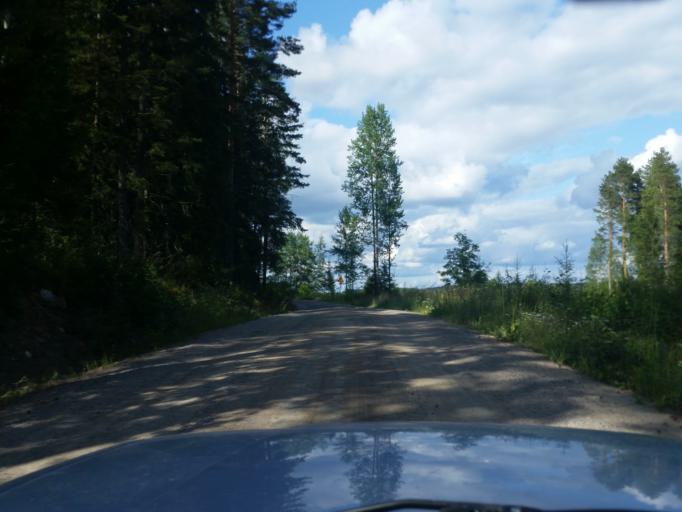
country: FI
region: Southern Savonia
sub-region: Savonlinna
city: Sulkava
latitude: 61.7055
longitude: 28.3022
